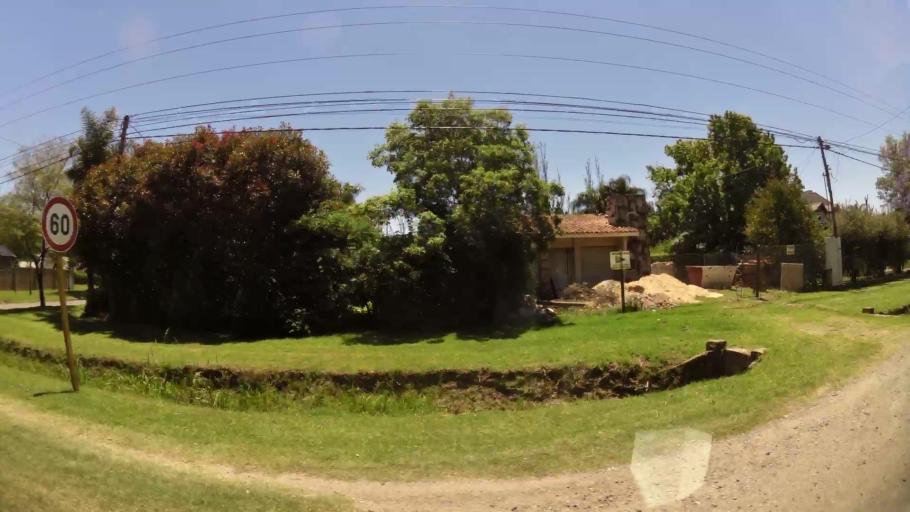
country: AR
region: Santa Fe
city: Rafaela
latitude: -31.2581
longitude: -61.4602
